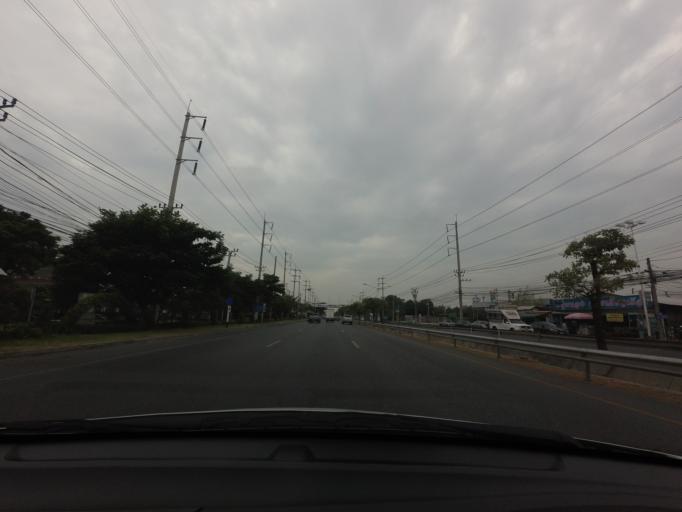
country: TH
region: Samut Prakan
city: Samut Prakan
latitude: 13.5523
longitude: 100.6152
